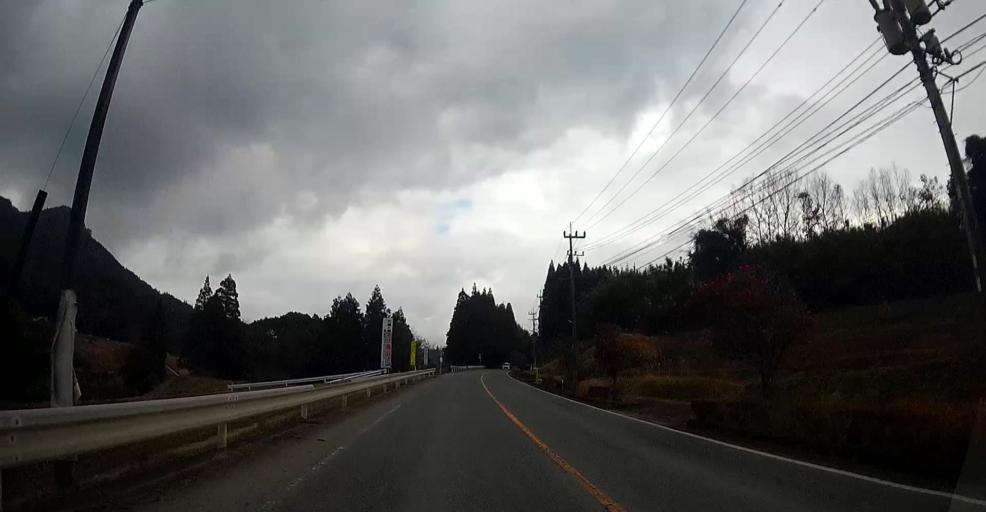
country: JP
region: Kumamoto
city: Matsubase
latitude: 32.6217
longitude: 130.8310
